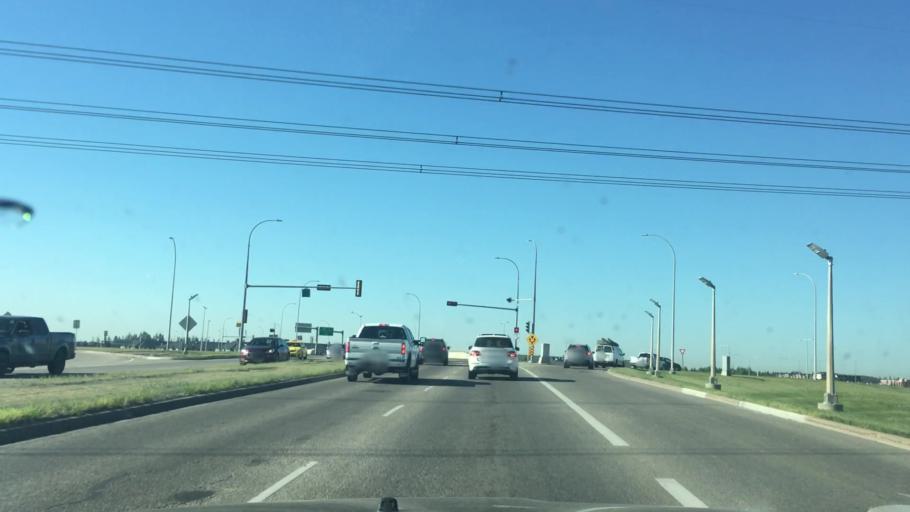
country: CA
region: Alberta
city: Edmonton
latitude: 53.4365
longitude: -113.5193
